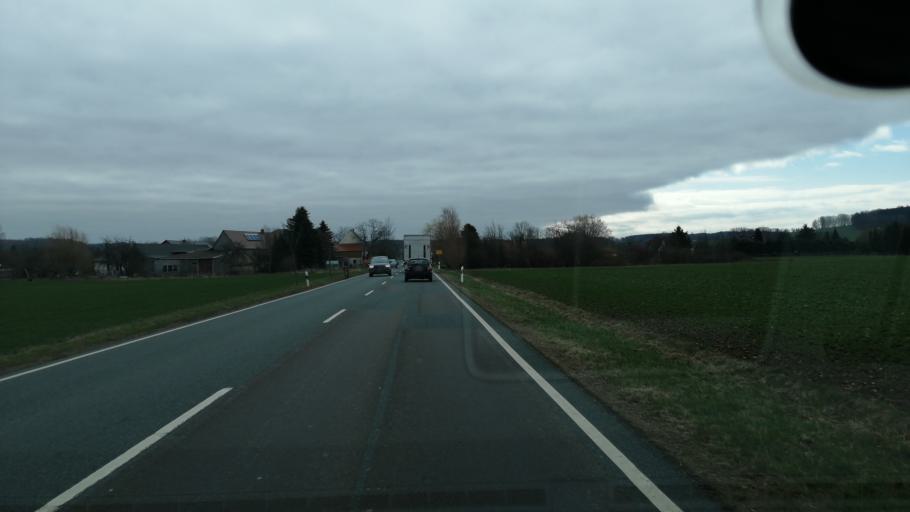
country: DE
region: Saxony
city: Niedercunnersdorf
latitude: 51.0667
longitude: 14.6877
